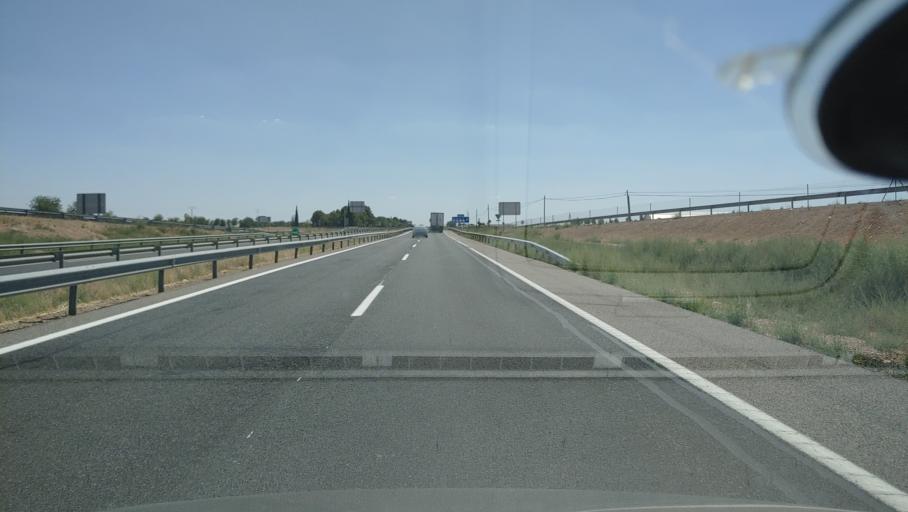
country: ES
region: Castille-La Mancha
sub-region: Provincia de Ciudad Real
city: Manzanares
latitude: 39.1225
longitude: -3.3778
